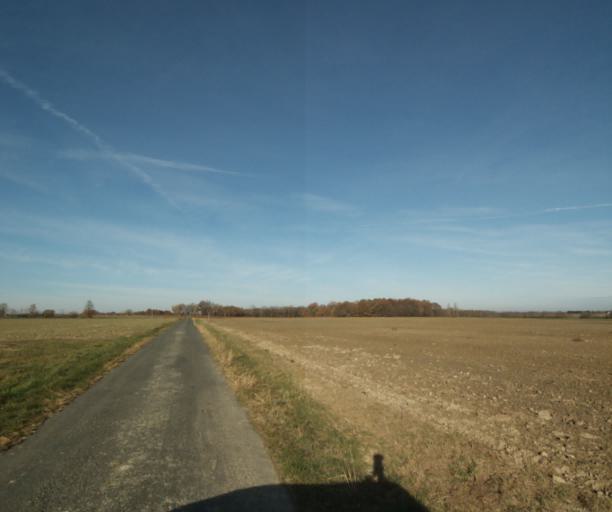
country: FR
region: Poitou-Charentes
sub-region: Departement de la Charente-Maritime
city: Cherac
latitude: 45.7478
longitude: -0.4797
